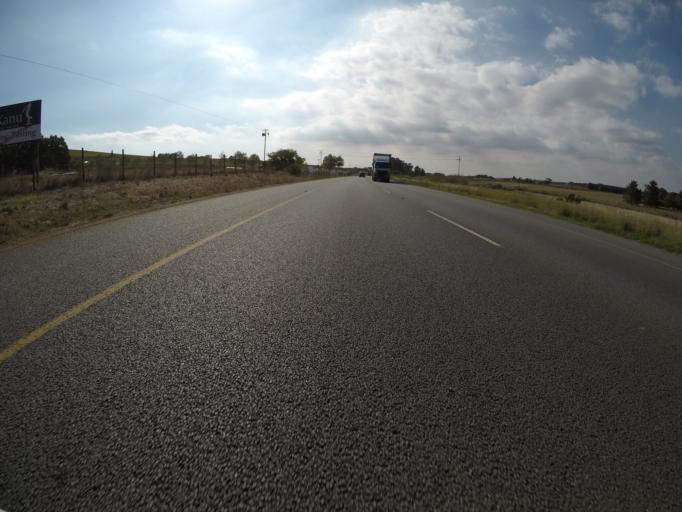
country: ZA
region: Western Cape
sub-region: Cape Winelands District Municipality
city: Stellenbosch
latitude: -33.8900
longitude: 18.8251
